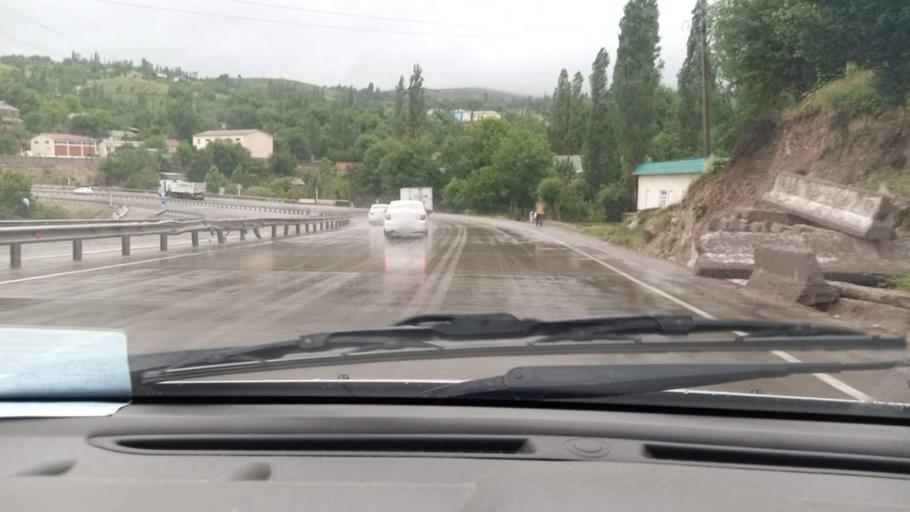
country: UZ
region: Toshkent
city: Angren
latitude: 41.0743
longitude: 70.2545
